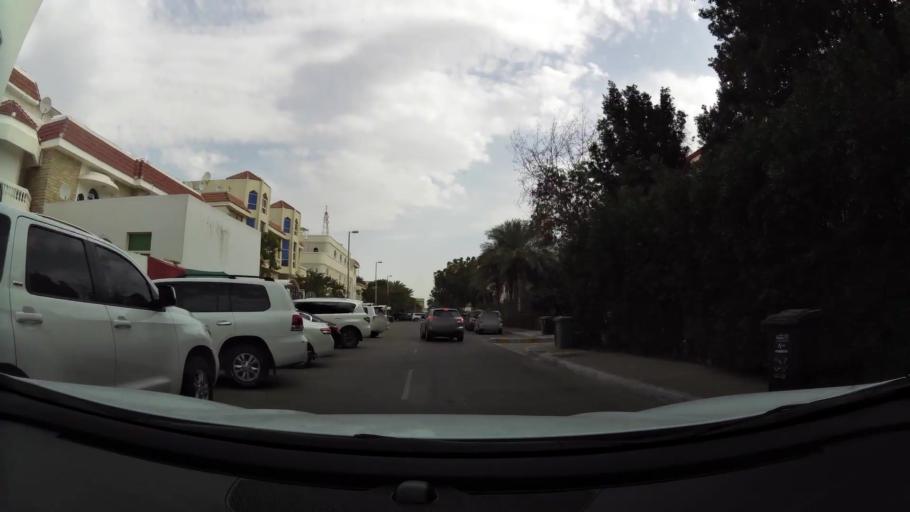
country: AE
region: Abu Dhabi
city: Abu Dhabi
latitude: 24.4625
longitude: 54.3512
